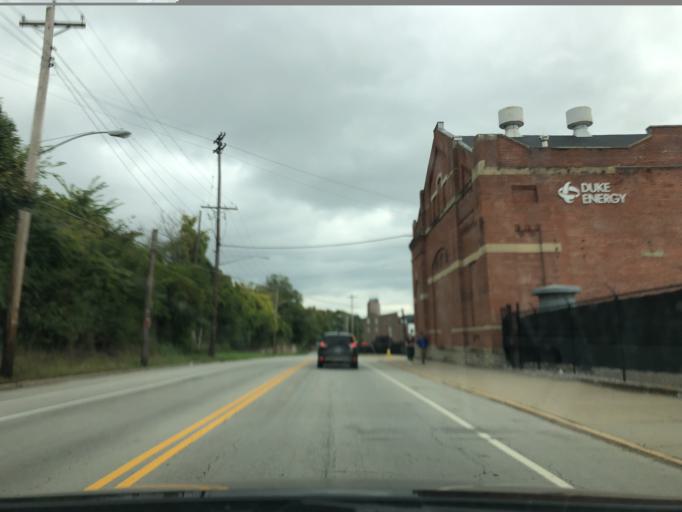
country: US
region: Kentucky
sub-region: Campbell County
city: Dayton
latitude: 39.1222
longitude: -84.4532
